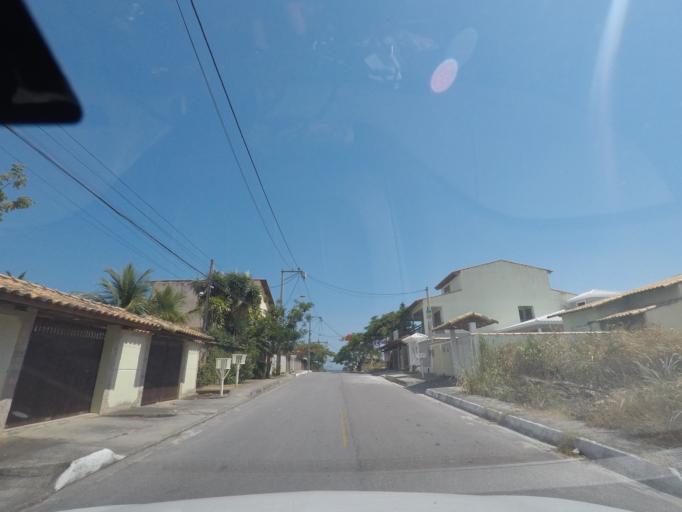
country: BR
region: Rio de Janeiro
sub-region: Marica
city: Marica
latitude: -22.9654
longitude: -42.9631
